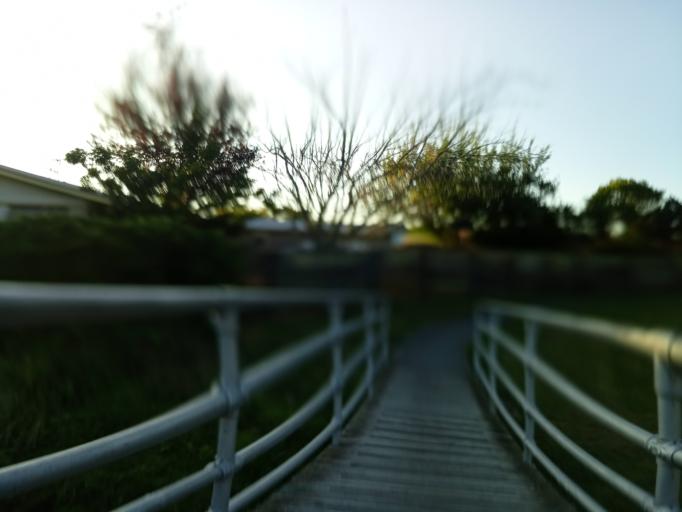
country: NZ
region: Gisborne
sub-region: Gisborne District
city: Gisborne
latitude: -38.6505
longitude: 178.0132
